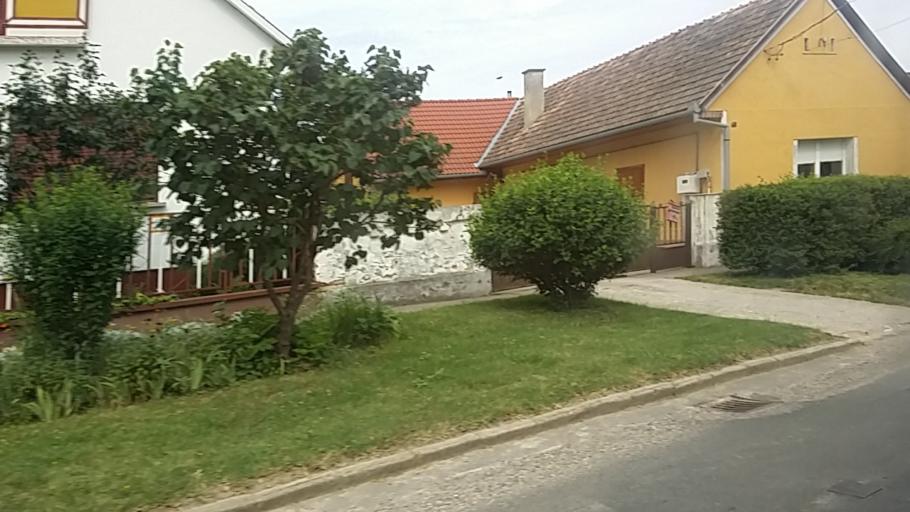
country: HU
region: Baranya
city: Villany
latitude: 45.9061
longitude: 18.4710
